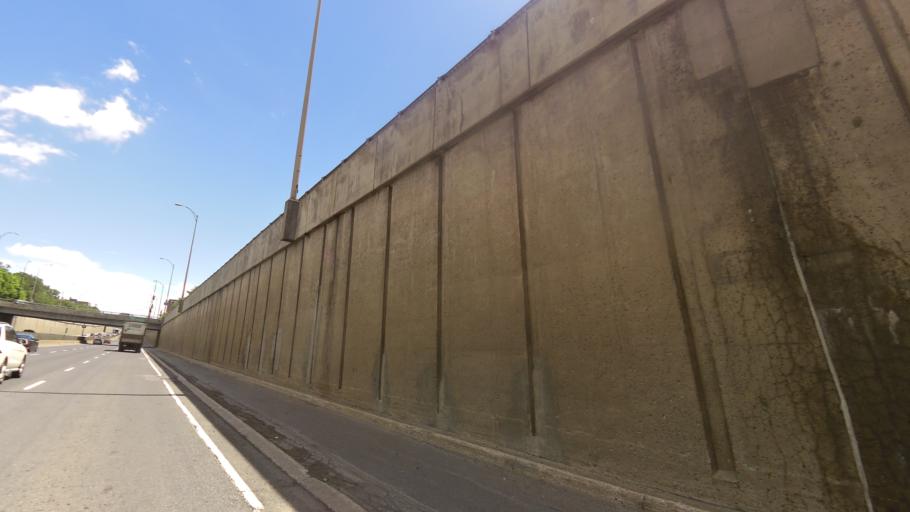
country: CA
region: Quebec
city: Saint-Raymond
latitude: 45.4833
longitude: -73.6286
